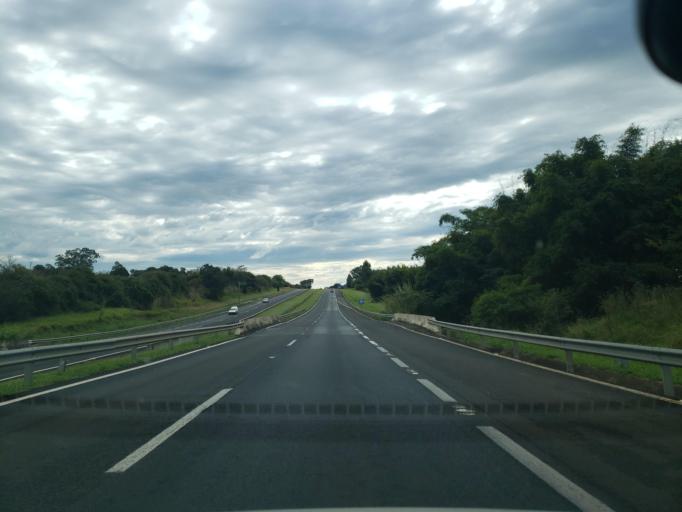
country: BR
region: Sao Paulo
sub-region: Bauru
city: Bauru
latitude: -22.2044
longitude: -49.1839
